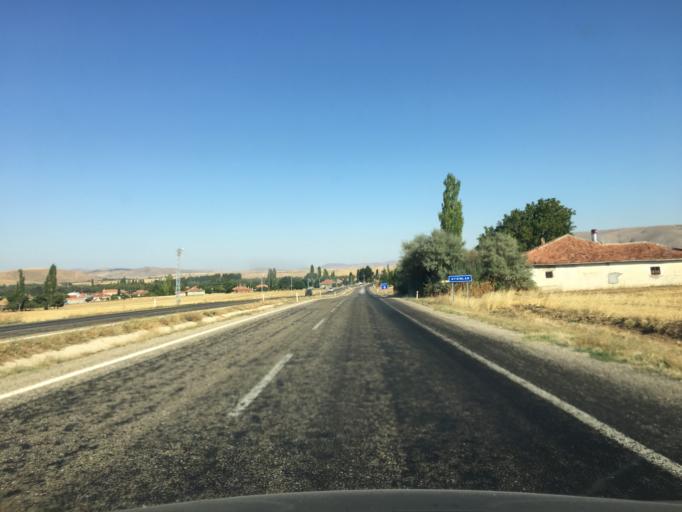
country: TR
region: Kirsehir
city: Akpinar
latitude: 39.3549
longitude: 33.9364
